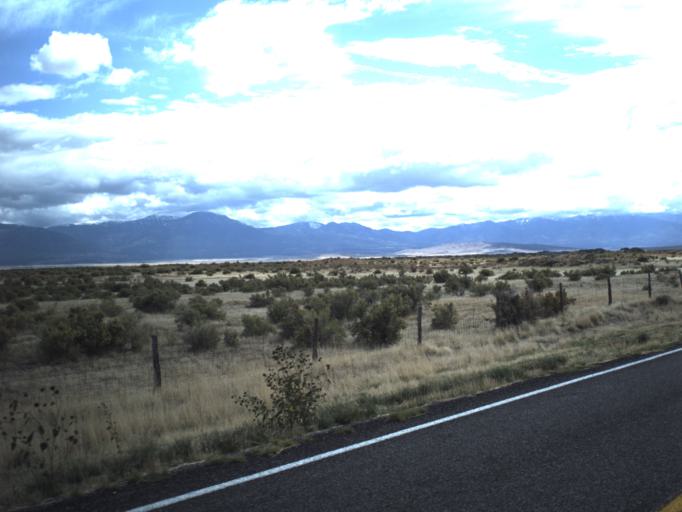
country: US
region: Utah
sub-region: Millard County
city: Fillmore
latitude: 39.1535
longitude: -112.4099
